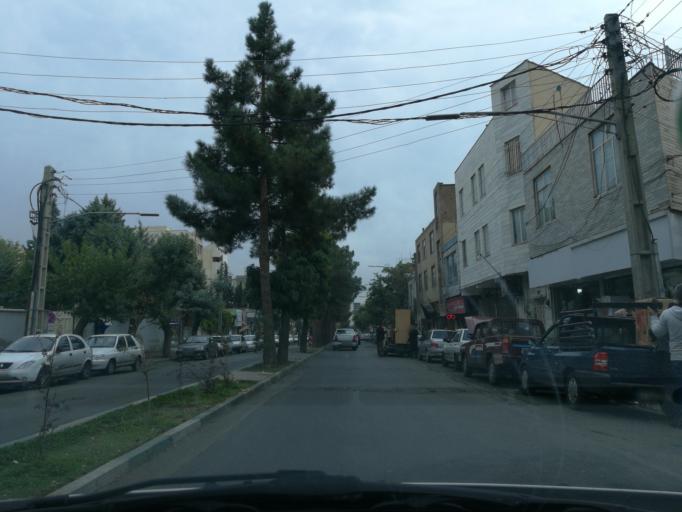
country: IR
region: Alborz
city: Karaj
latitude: 35.8471
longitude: 50.9694
